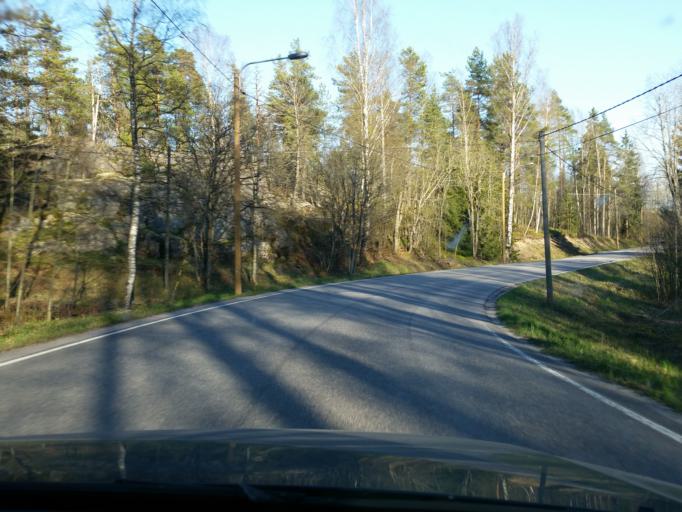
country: FI
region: Uusimaa
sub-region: Helsinki
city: Kirkkonummi
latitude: 60.1233
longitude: 24.5249
